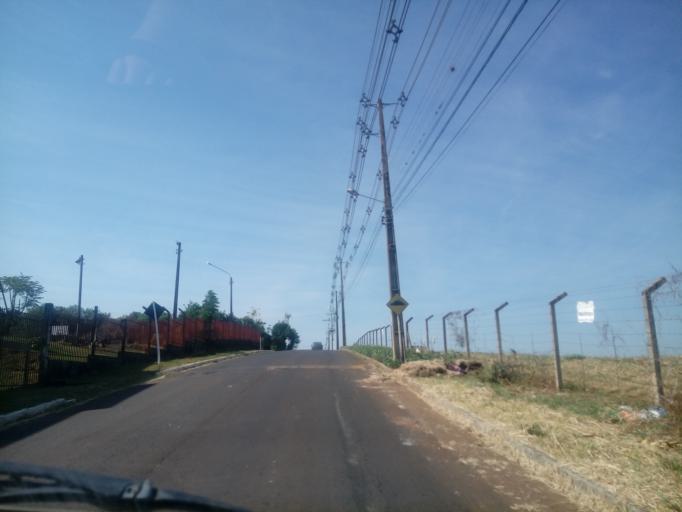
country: BR
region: Santa Catarina
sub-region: Chapeco
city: Chapeco
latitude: -27.0836
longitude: -52.6341
